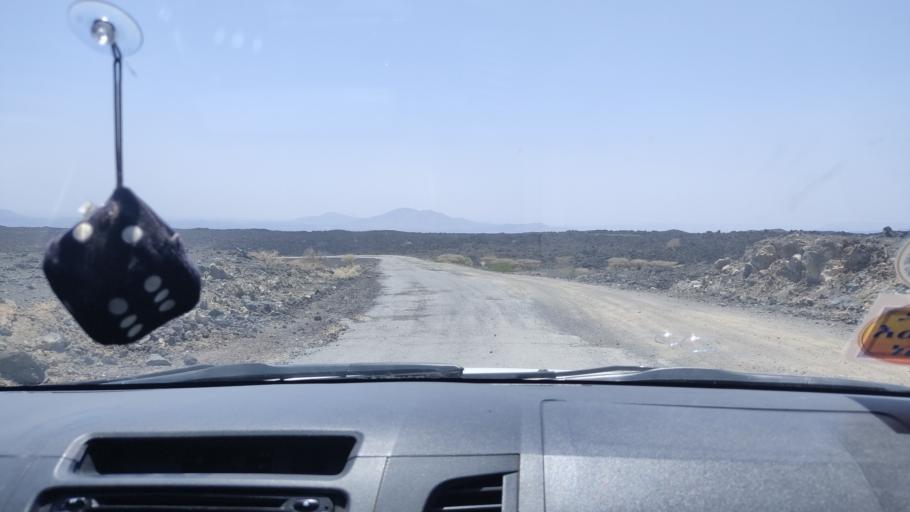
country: DJ
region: Tadjourah
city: Dorra
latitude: 12.3965
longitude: 42.1741
